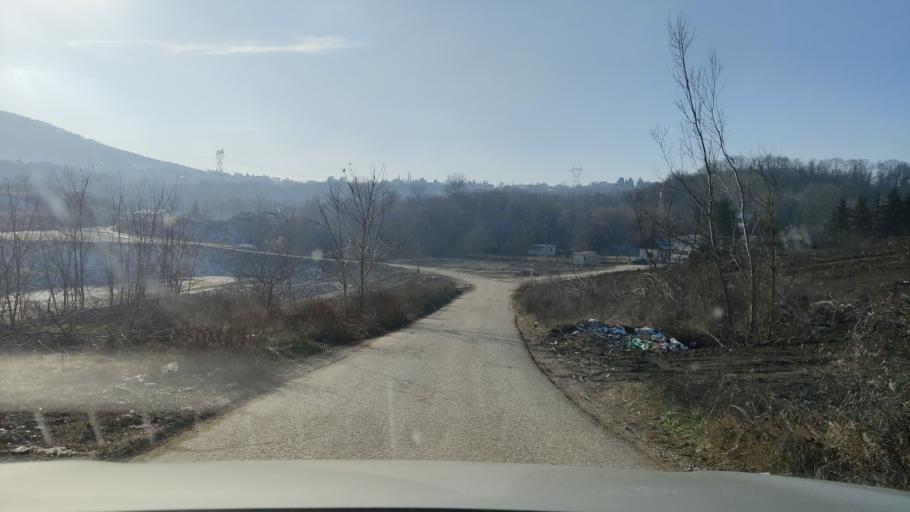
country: RS
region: Central Serbia
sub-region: Belgrade
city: Zvezdara
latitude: 44.7165
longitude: 20.5171
